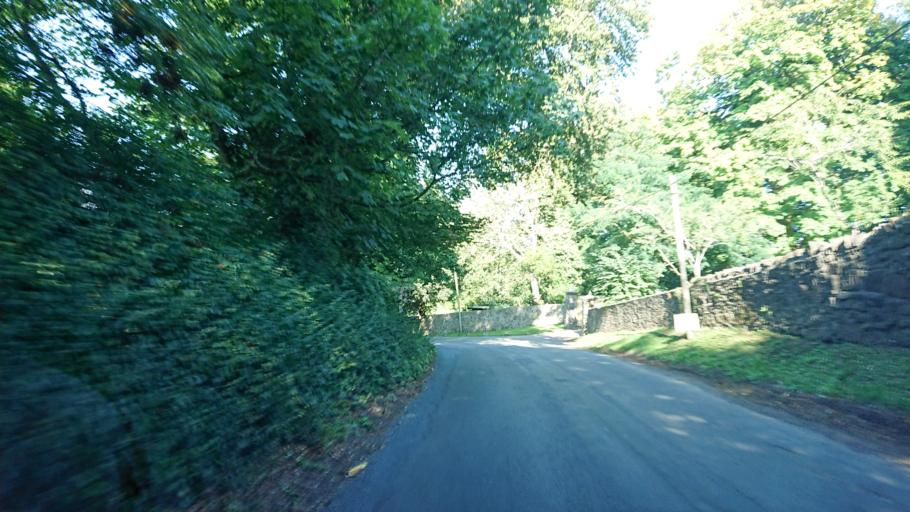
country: IE
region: Munster
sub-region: Waterford
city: Dunmore East
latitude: 52.1896
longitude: -6.9890
